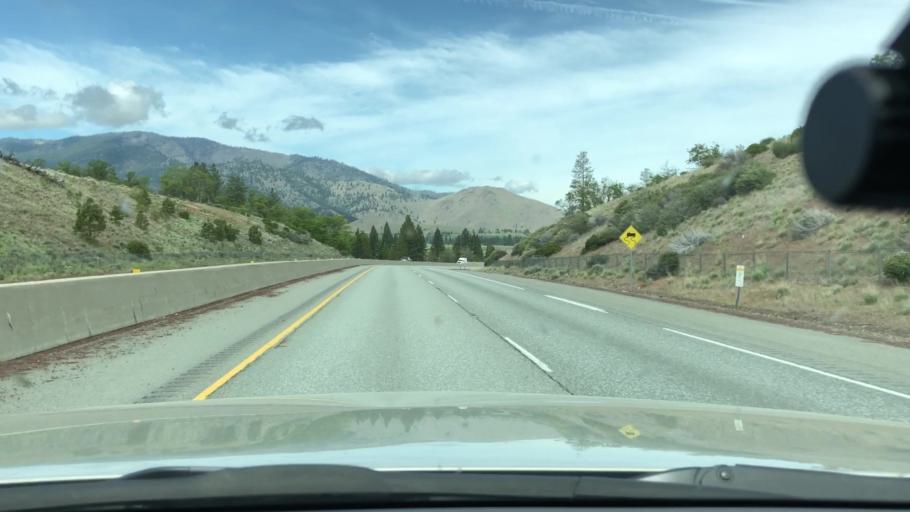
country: US
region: California
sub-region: Siskiyou County
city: Weed
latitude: 41.4297
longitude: -122.4256
